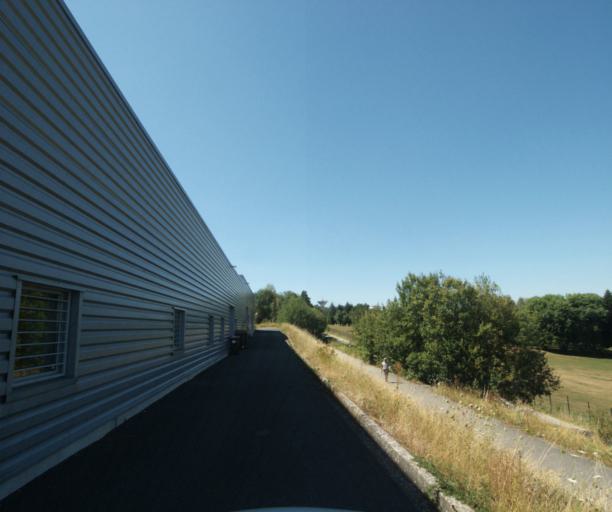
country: FR
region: Lorraine
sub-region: Departement des Vosges
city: Epinal
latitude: 48.1904
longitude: 6.4711
